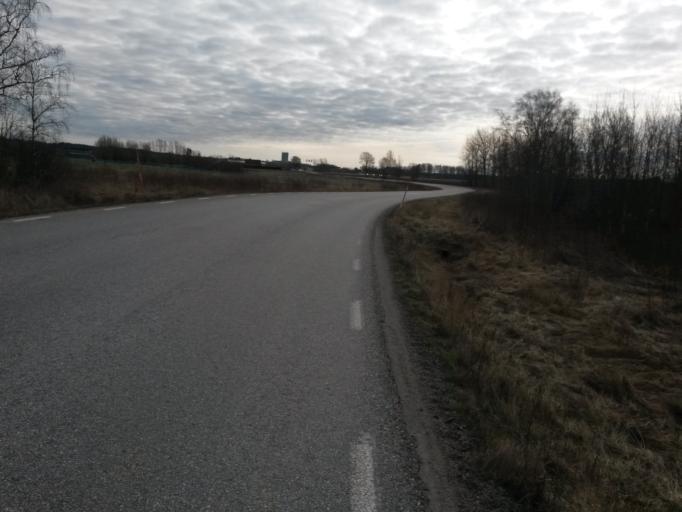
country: SE
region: Vaestra Goetaland
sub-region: Herrljunga Kommun
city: Herrljunga
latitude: 58.0906
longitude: 13.0046
